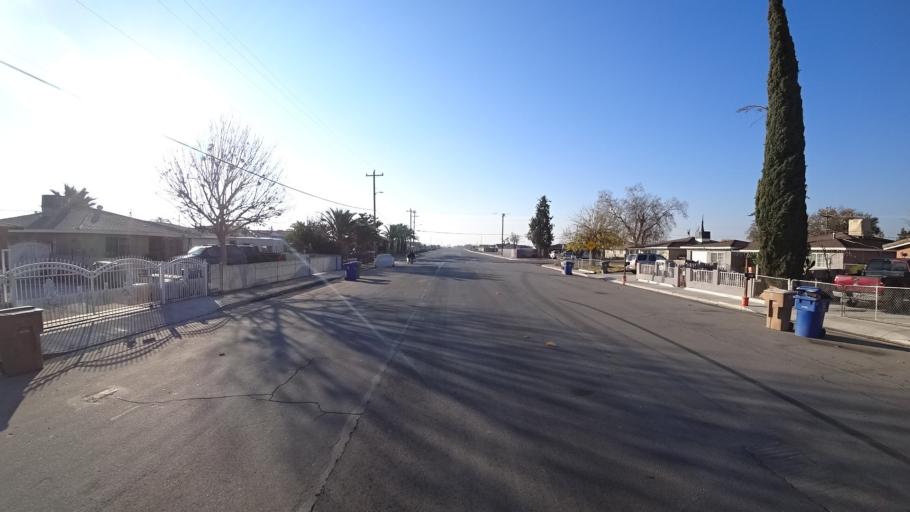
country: US
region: California
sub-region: Kern County
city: Greenfield
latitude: 35.3003
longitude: -118.9943
